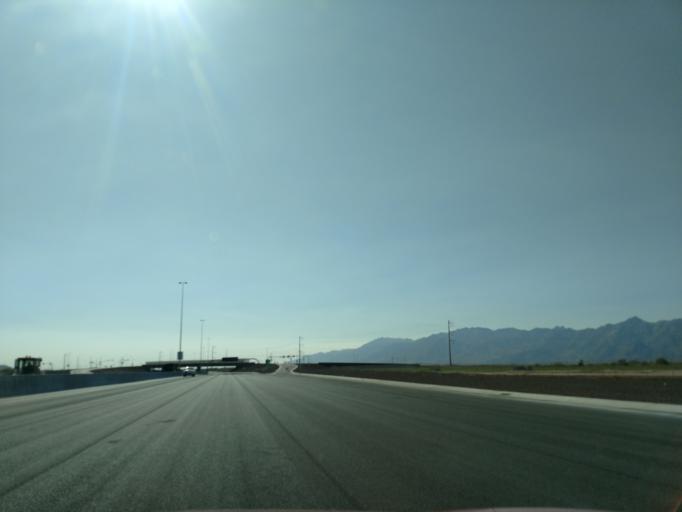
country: US
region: Arizona
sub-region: Maricopa County
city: Laveen
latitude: 33.3530
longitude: -112.1914
